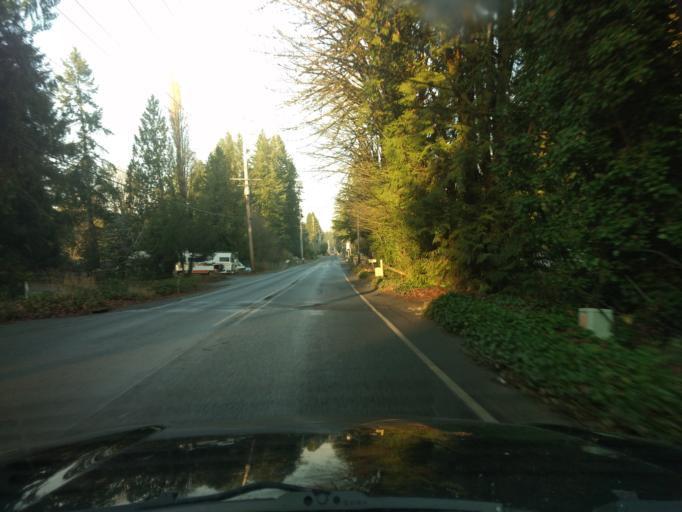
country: US
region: Washington
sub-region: Kitsap County
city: Erlands Point-Kitsap Lake
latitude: 47.5817
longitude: -122.7150
